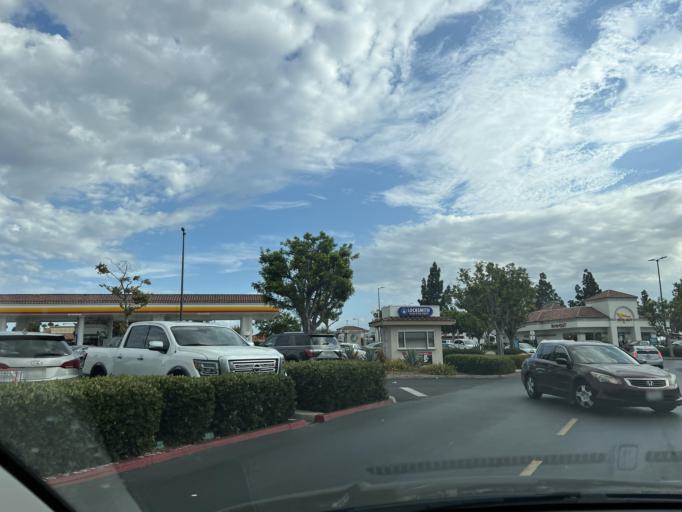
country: US
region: California
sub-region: San Diego County
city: Poway
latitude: 32.9184
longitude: -117.1214
